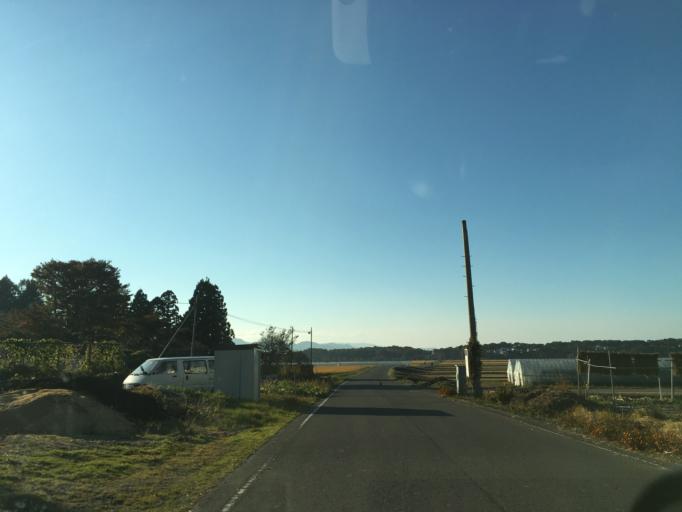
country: JP
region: Fukushima
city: Inawashiro
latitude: 37.4162
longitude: 140.1386
